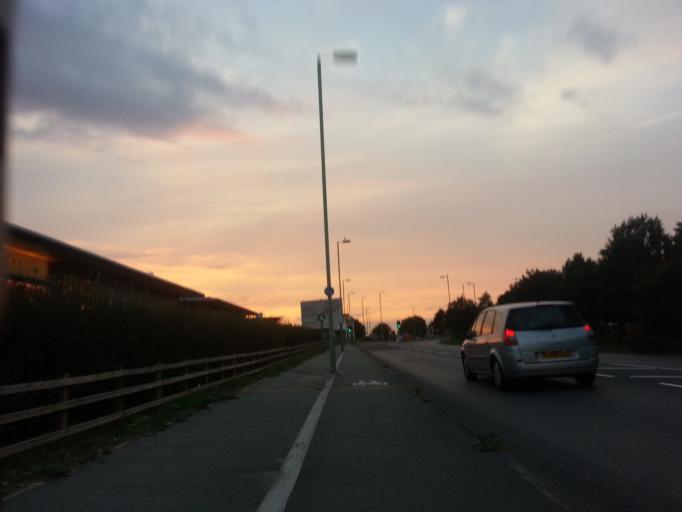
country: GB
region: England
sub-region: Suffolk
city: Kesgrave
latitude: 52.0285
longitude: 1.2033
